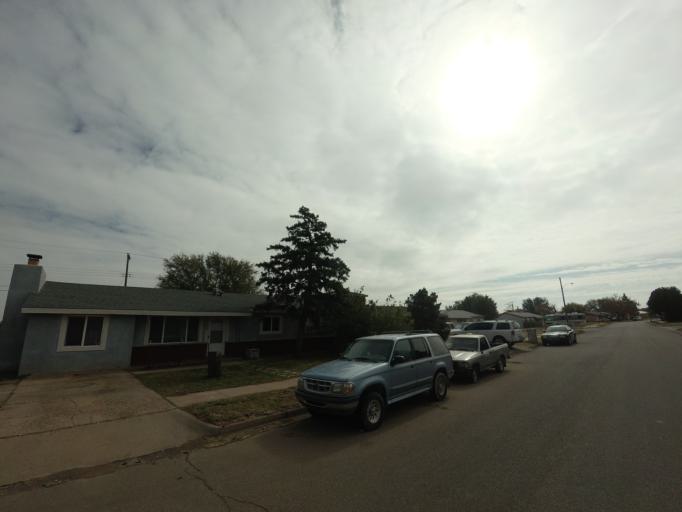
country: US
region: New Mexico
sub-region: Curry County
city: Clovis
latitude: 34.4294
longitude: -103.2167
